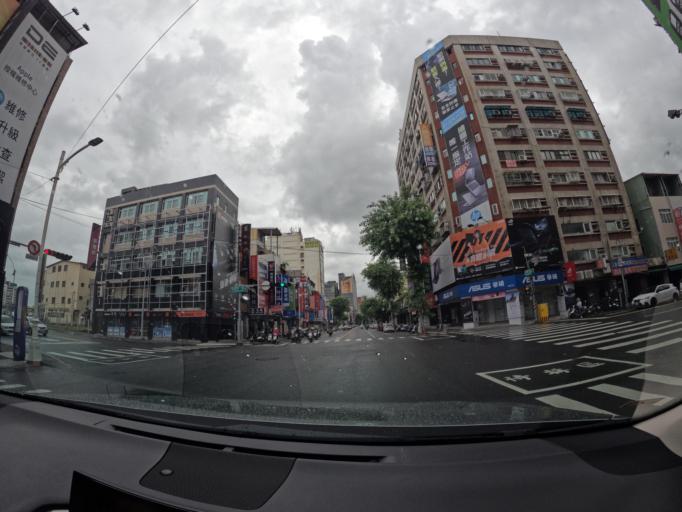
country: TW
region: Kaohsiung
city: Kaohsiung
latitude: 22.6374
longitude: 120.3084
